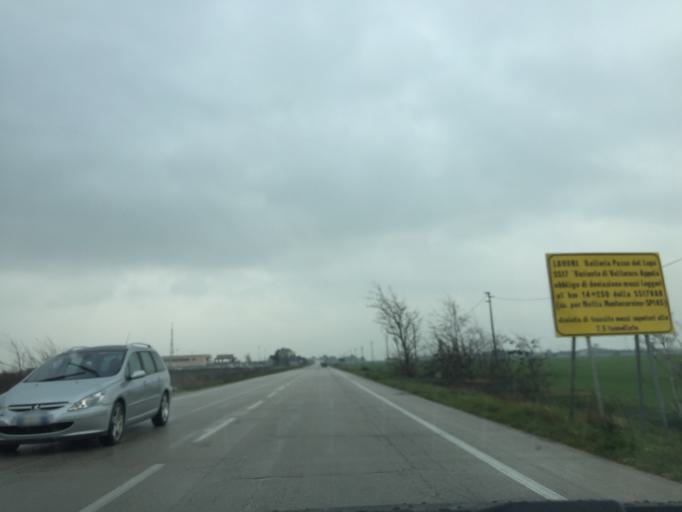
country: IT
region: Apulia
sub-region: Provincia di Foggia
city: Foggia
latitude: 41.4818
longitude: 15.5171
